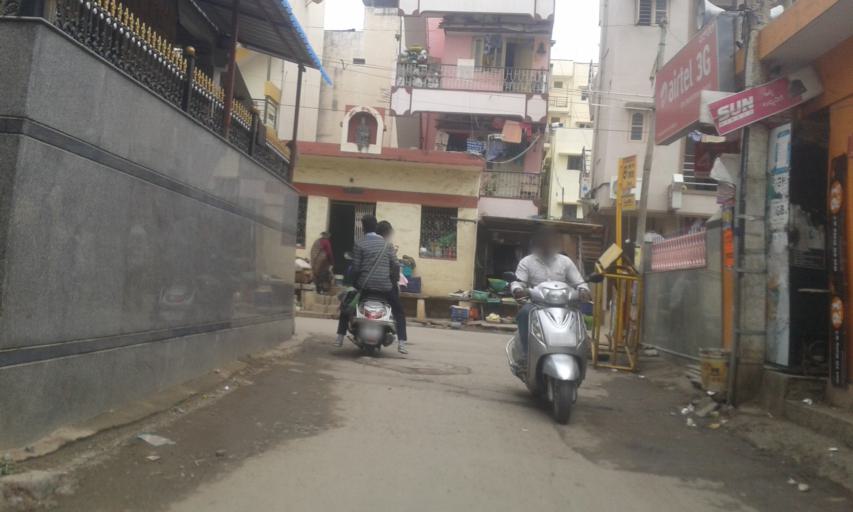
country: IN
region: Karnataka
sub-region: Bangalore Urban
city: Bangalore
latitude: 12.9636
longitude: 77.6471
